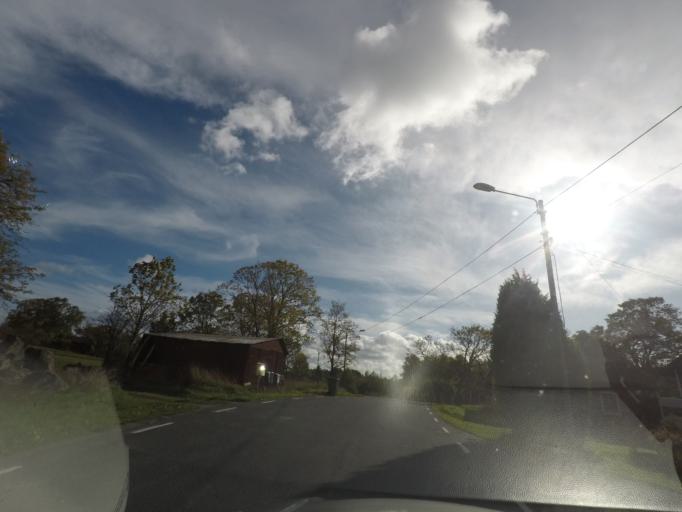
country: SE
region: Soedermanland
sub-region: Eskilstuna Kommun
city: Kvicksund
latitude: 59.3160
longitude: 16.2484
